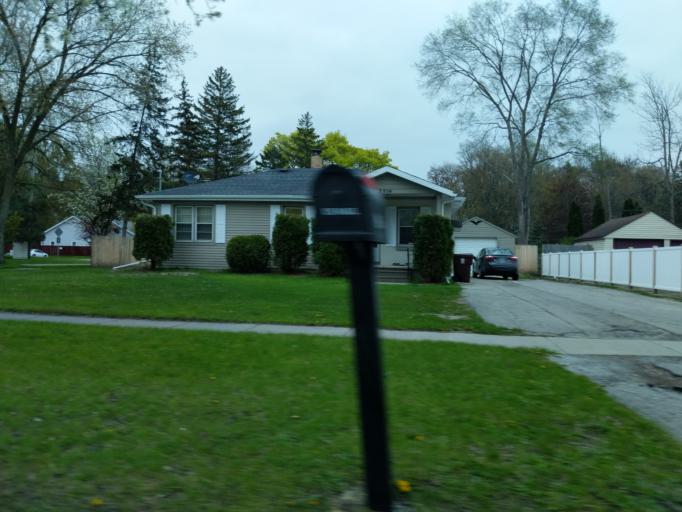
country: US
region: Michigan
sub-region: Midland County
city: Midland
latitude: 43.6336
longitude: -84.2269
